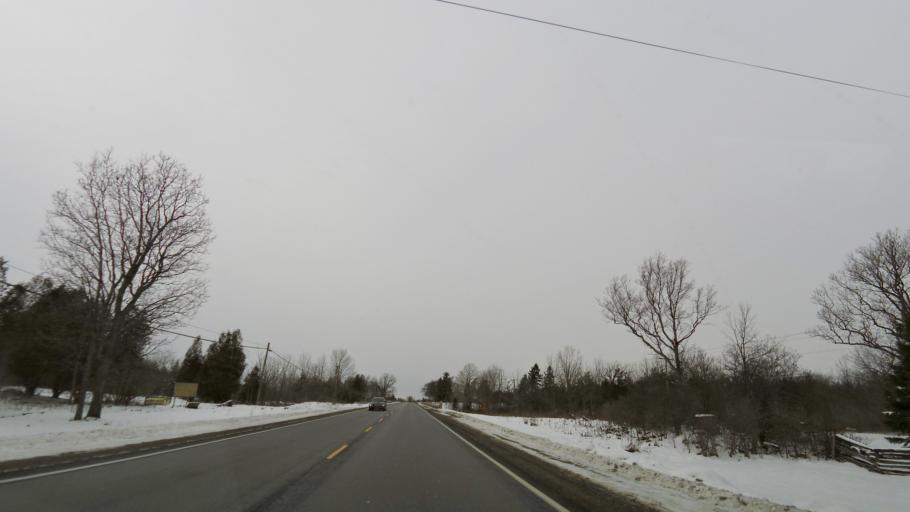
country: CA
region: Ontario
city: Cambridge
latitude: 43.3137
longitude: -80.1656
